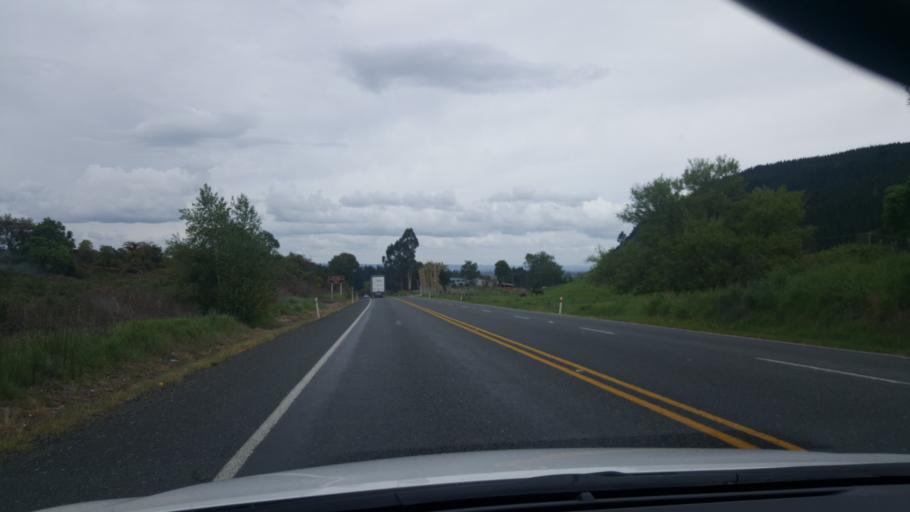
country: NZ
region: Bay of Plenty
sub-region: Rotorua District
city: Rotorua
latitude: -38.3472
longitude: 176.3611
